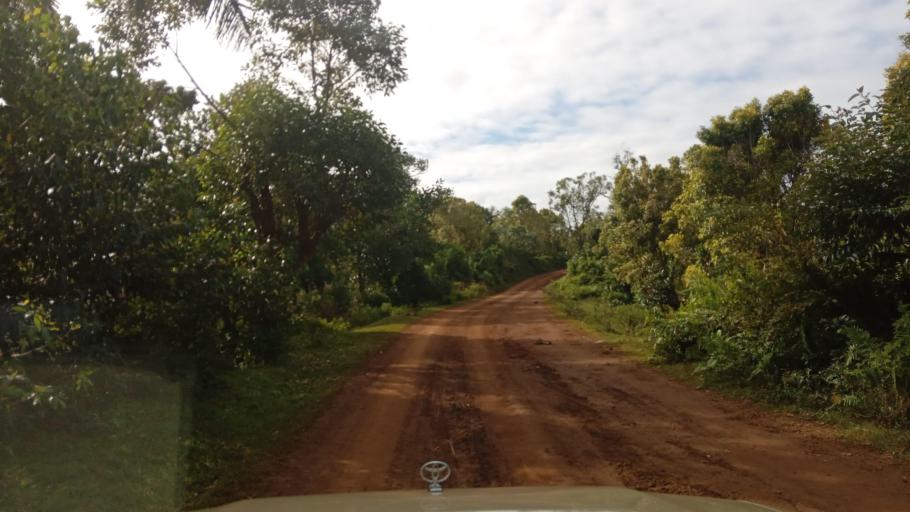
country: MG
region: Atsimo-Atsinanana
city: Vohipaho
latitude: -23.7474
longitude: 47.5569
